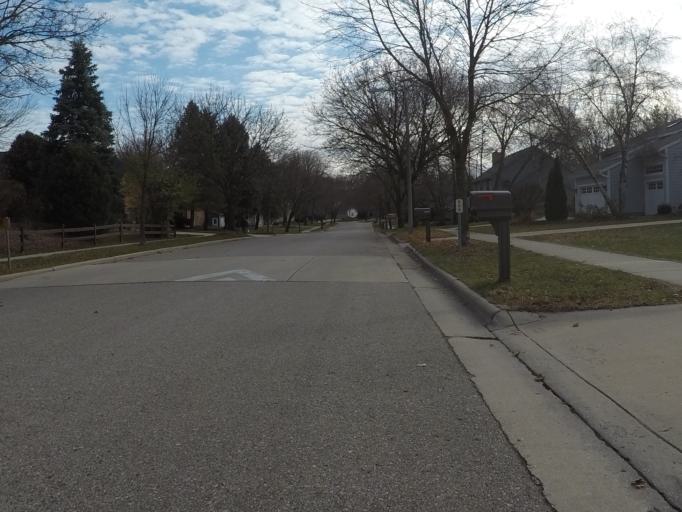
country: US
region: Wisconsin
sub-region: Dane County
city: Middleton
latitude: 43.0743
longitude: -89.5164
